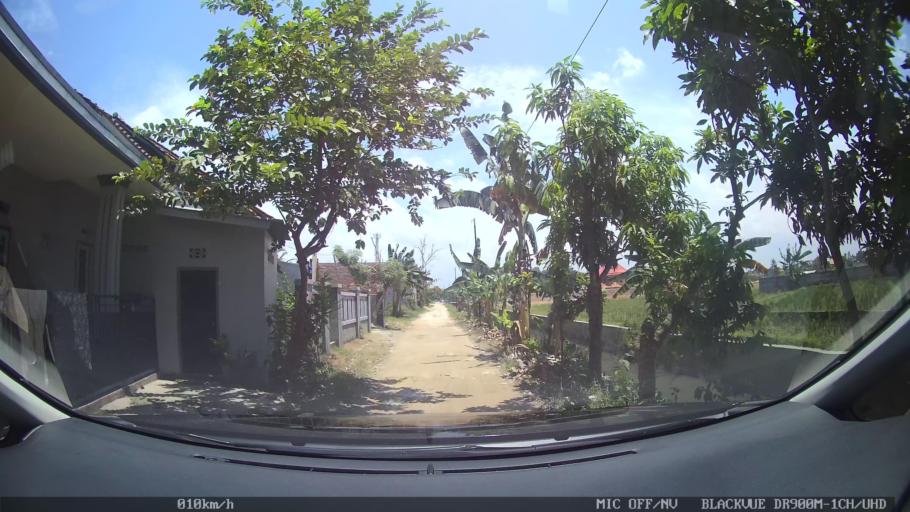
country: ID
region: Lampung
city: Kedaton
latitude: -5.3724
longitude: 105.2921
